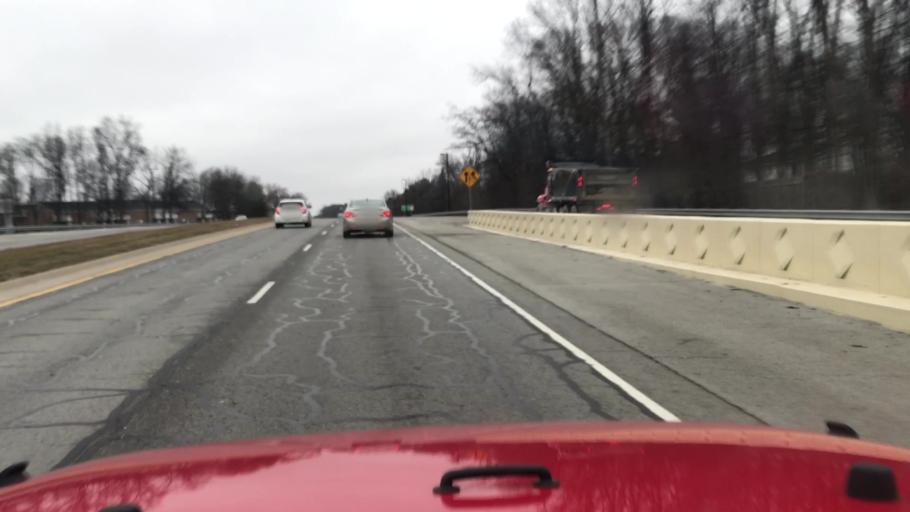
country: US
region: Indiana
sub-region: Hamilton County
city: Carmel
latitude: 39.9638
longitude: -86.1133
